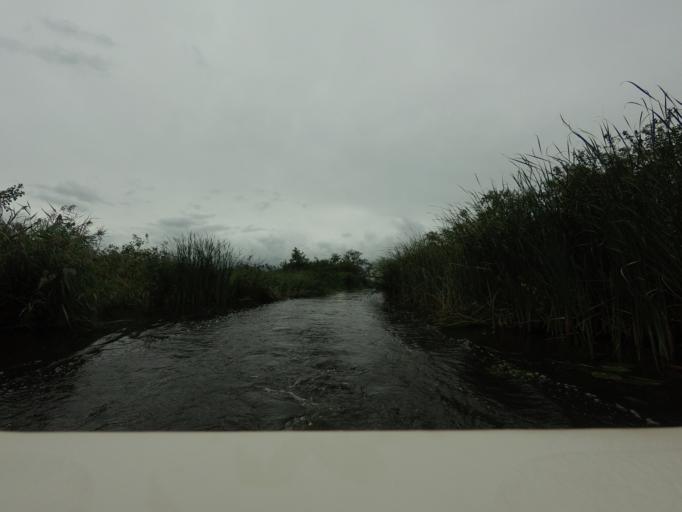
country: NL
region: Friesland
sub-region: Gemeente Boarnsterhim
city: Warten
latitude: 53.1234
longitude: 5.9293
